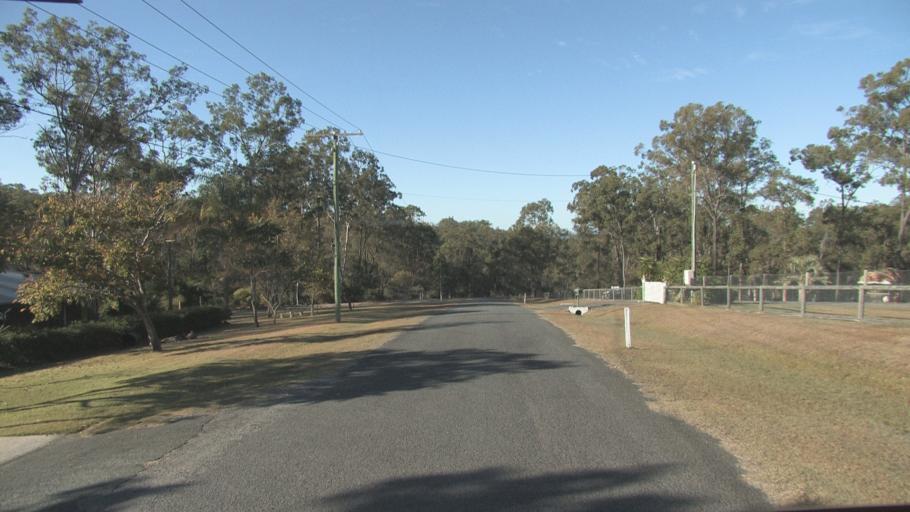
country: AU
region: Queensland
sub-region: Logan
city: Cedar Vale
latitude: -27.8355
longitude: 153.0882
